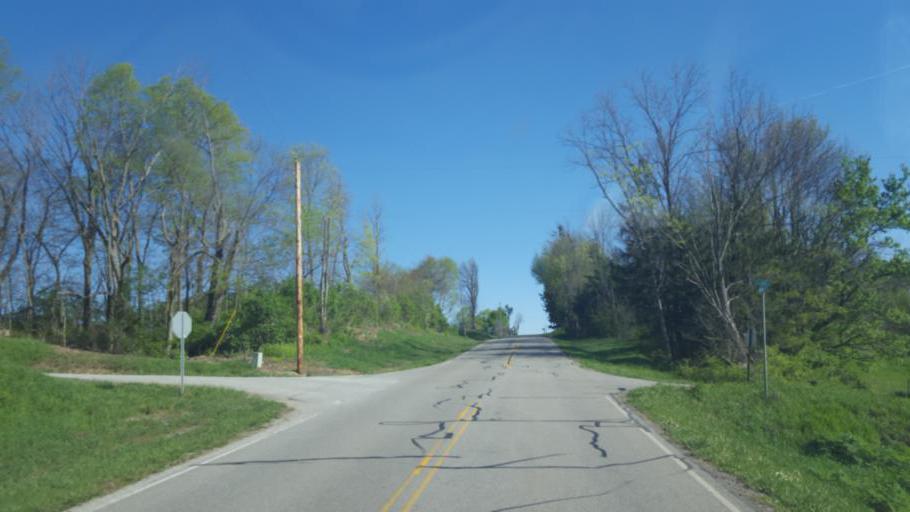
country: US
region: Ohio
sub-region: Crawford County
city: Bucyrus
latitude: 40.7459
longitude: -83.0925
